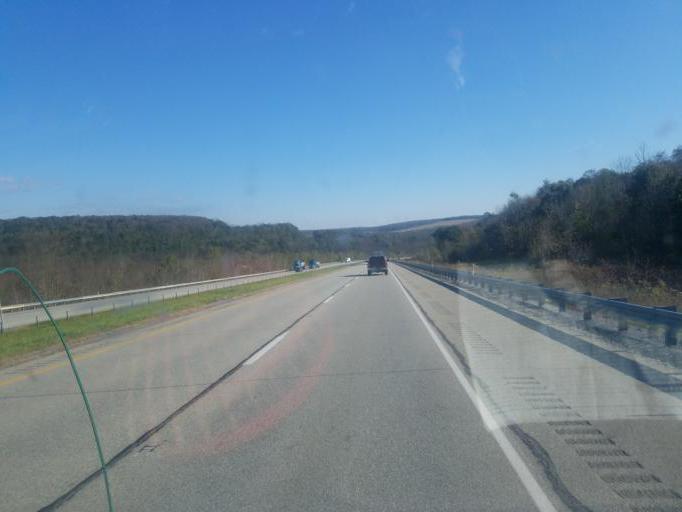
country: US
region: Pennsylvania
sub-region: Cambria County
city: Gallitzin
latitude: 40.4744
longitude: -78.5310
